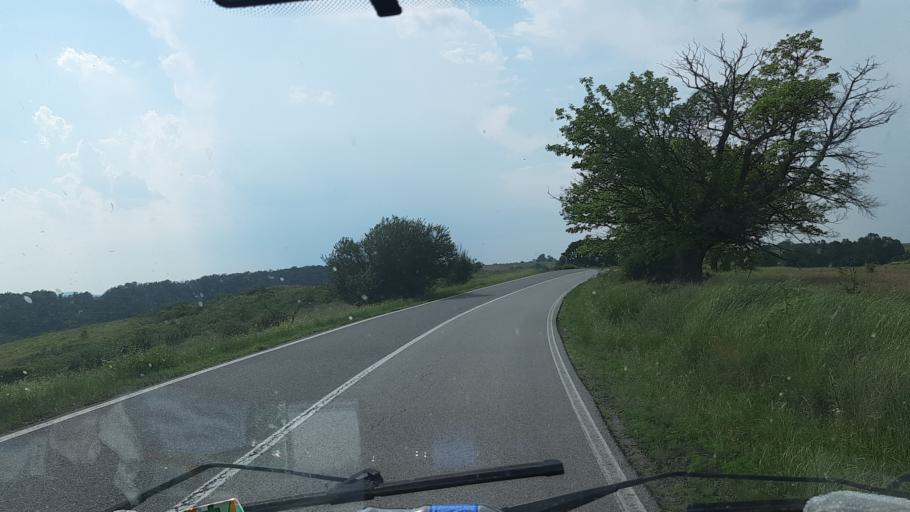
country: RO
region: Caras-Severin
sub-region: Comuna Farliug
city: Farliug
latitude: 45.5456
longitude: 21.8731
